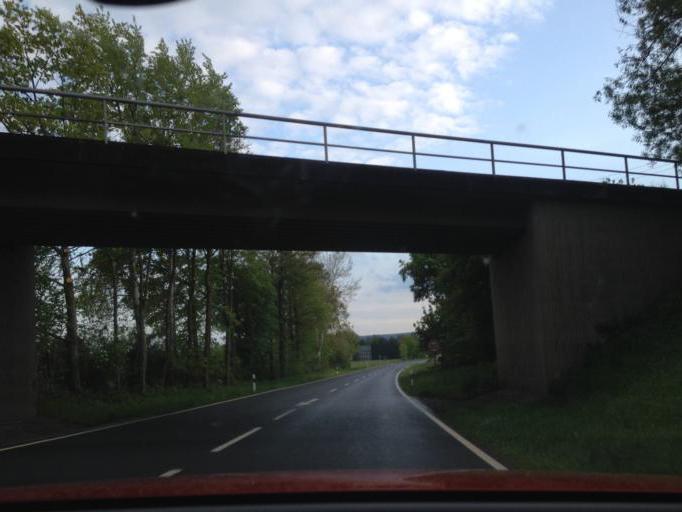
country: DE
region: Bavaria
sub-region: Upper Palatinate
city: Etzenricht
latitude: 49.6293
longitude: 12.1010
